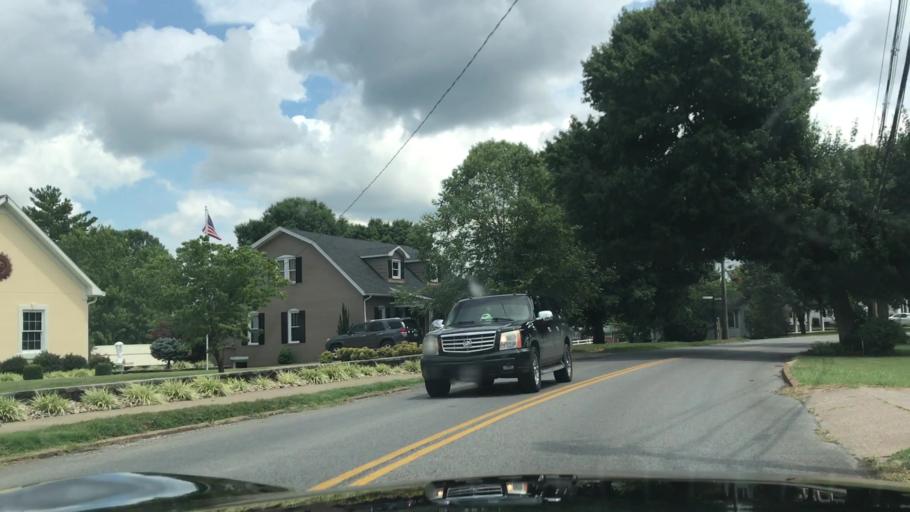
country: US
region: Kentucky
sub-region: Muhlenberg County
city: Greenville
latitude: 37.2052
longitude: -87.1705
